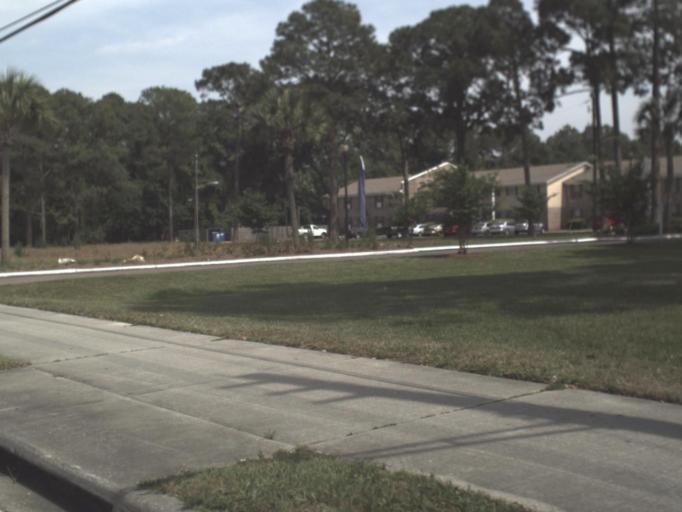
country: US
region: Florida
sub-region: Clay County
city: Bellair-Meadowbrook Terrace
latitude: 30.2480
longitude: -81.7825
